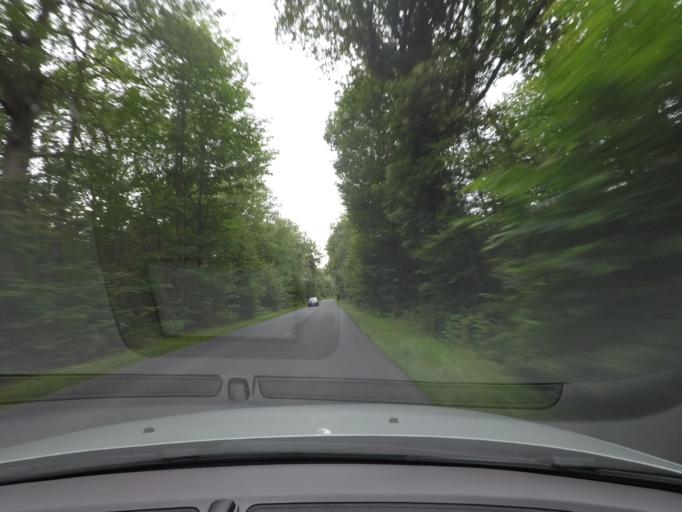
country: FR
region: Haute-Normandie
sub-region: Departement de la Seine-Maritime
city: Ymare
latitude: 49.3366
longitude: 1.1939
